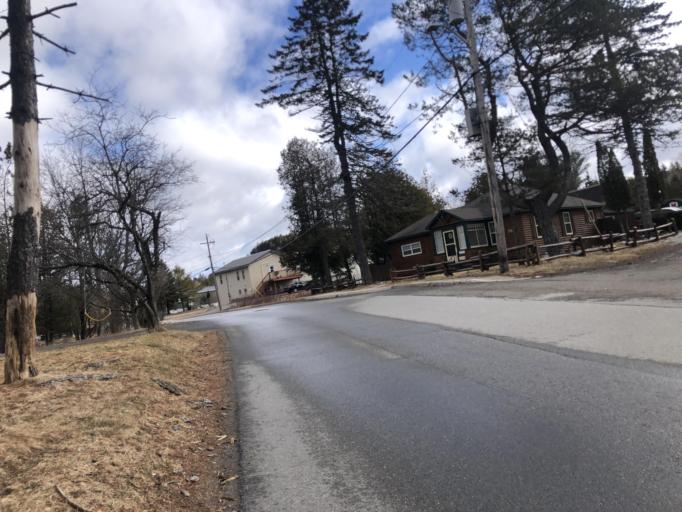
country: CA
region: New Brunswick
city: Saint John
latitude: 45.3236
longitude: -66.0134
